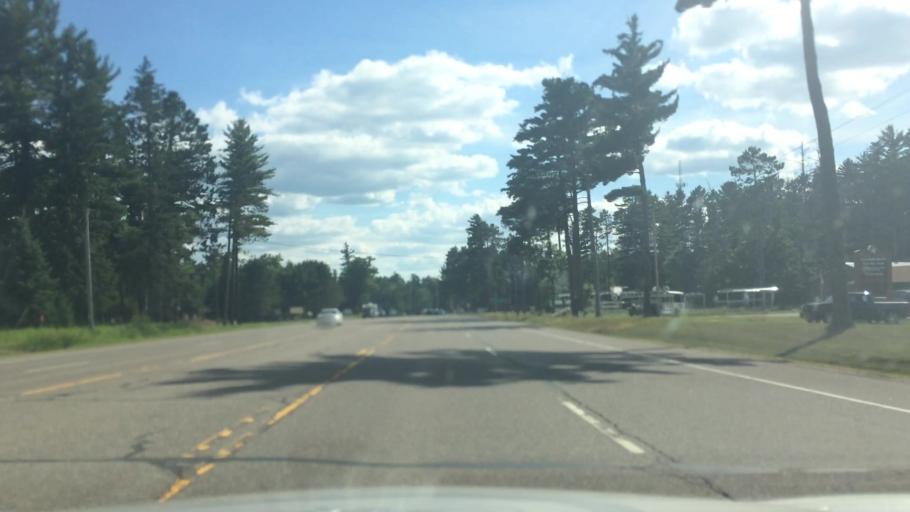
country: US
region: Wisconsin
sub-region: Vilas County
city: Lac du Flambeau
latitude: 45.8238
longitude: -89.7229
